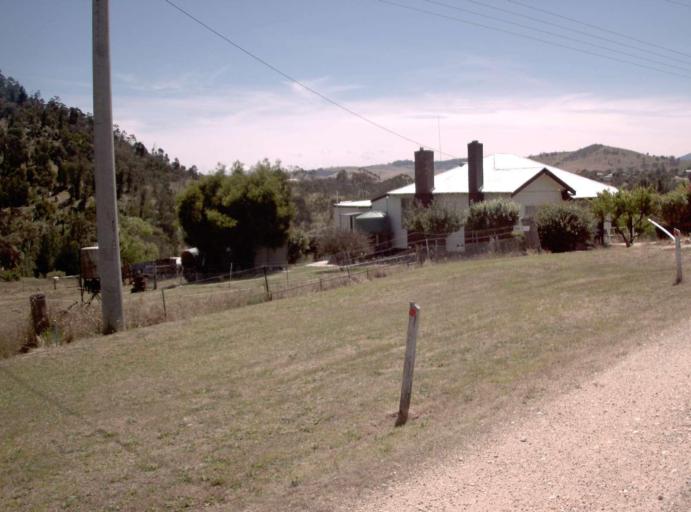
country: AU
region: Victoria
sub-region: Alpine
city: Mount Beauty
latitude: -37.1029
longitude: 147.5845
